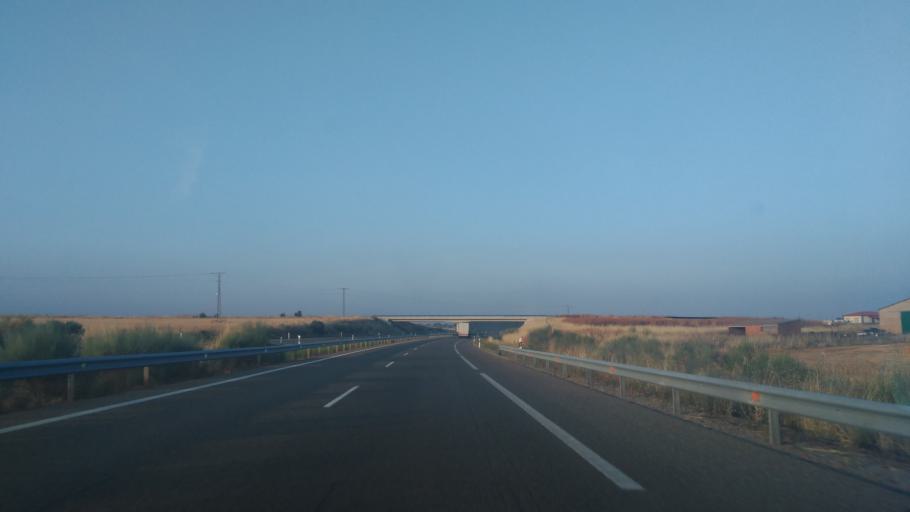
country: ES
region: Castille and Leon
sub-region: Provincia de Salamanca
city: Galindo y Perahuy
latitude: 40.9122
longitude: -5.8648
